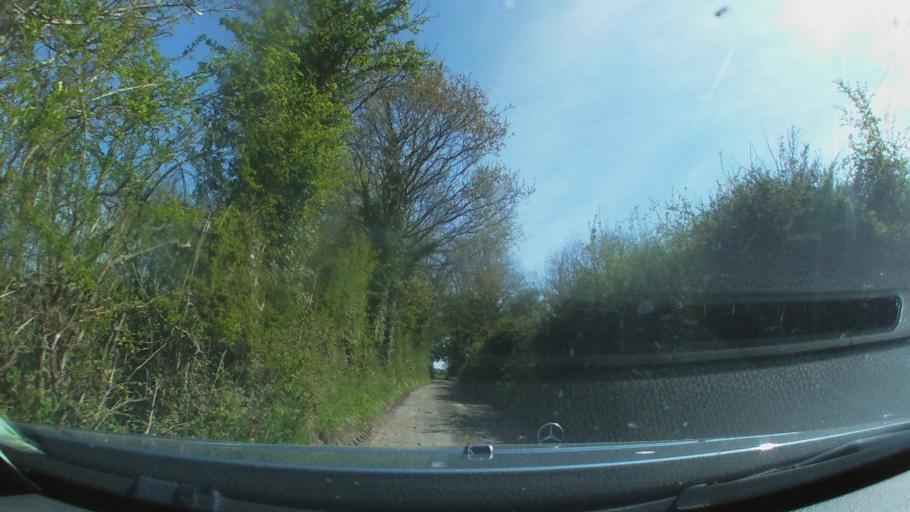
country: IE
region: Leinster
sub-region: Kilkenny
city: Callan
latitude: 52.6008
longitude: -7.3913
